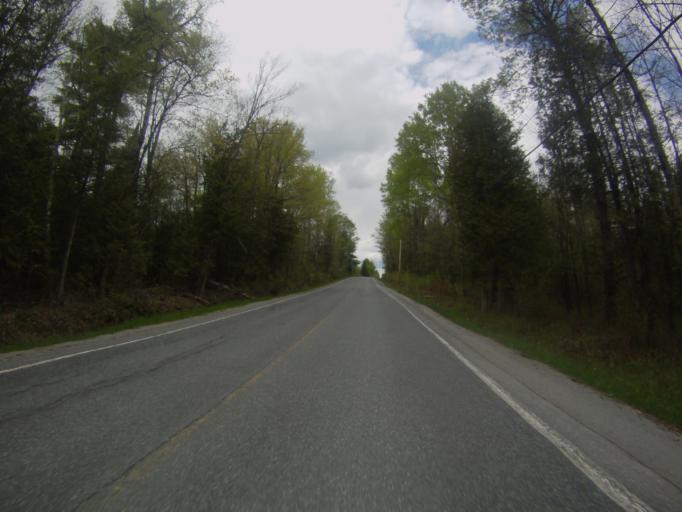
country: US
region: New York
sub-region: Essex County
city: Port Henry
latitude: 44.0023
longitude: -73.4966
